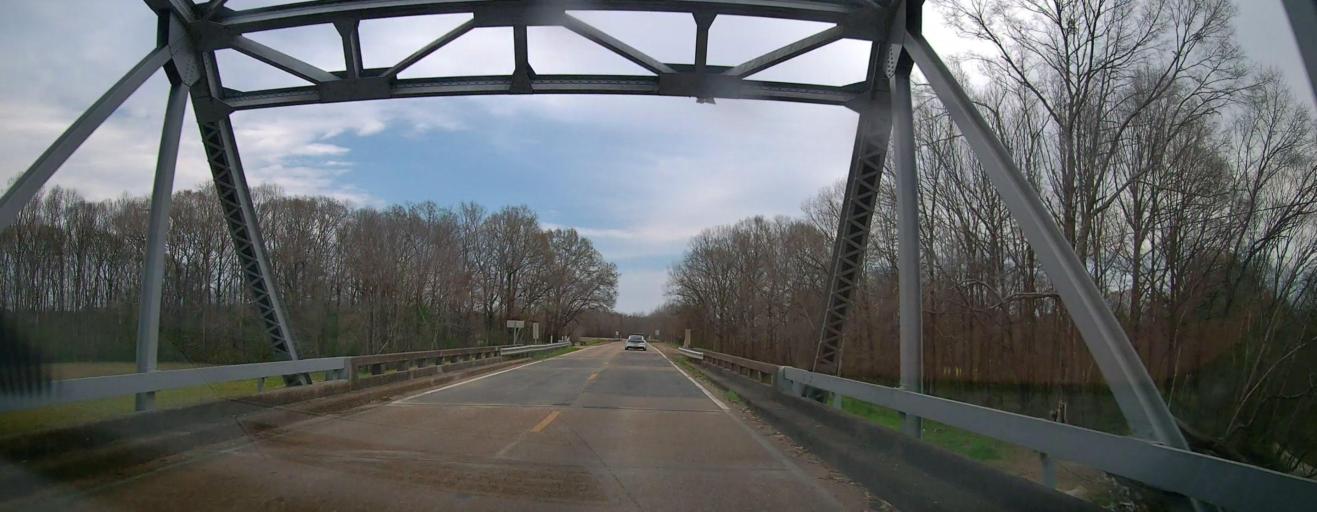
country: US
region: Mississippi
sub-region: Itawamba County
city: Fulton
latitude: 34.2525
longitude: -88.4763
